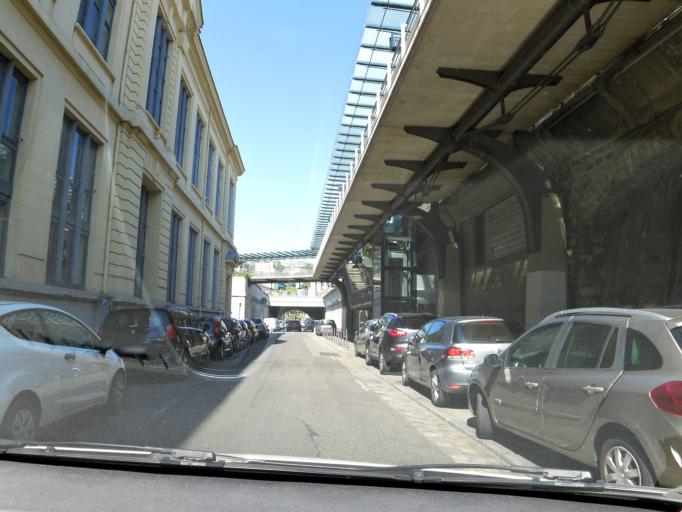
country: FR
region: Rhone-Alpes
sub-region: Departement du Rhone
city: Lyon
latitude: 45.7479
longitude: 4.8246
